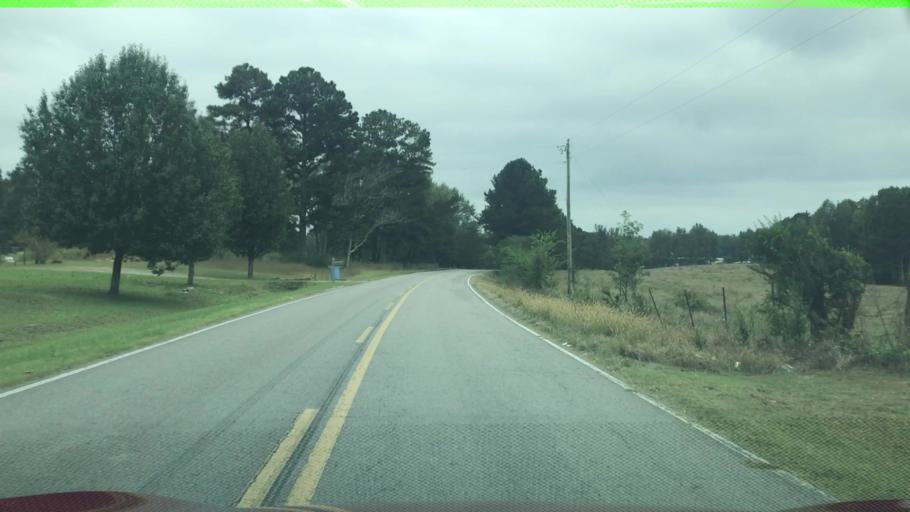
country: US
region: Alabama
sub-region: Cullman County
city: Good Hope
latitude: 34.1045
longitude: -87.0369
